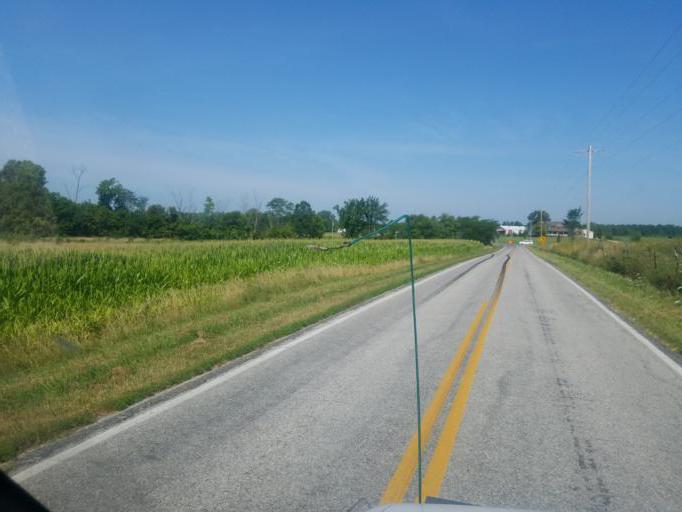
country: US
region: Ohio
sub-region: Union County
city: New California
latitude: 40.2828
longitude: -83.2302
